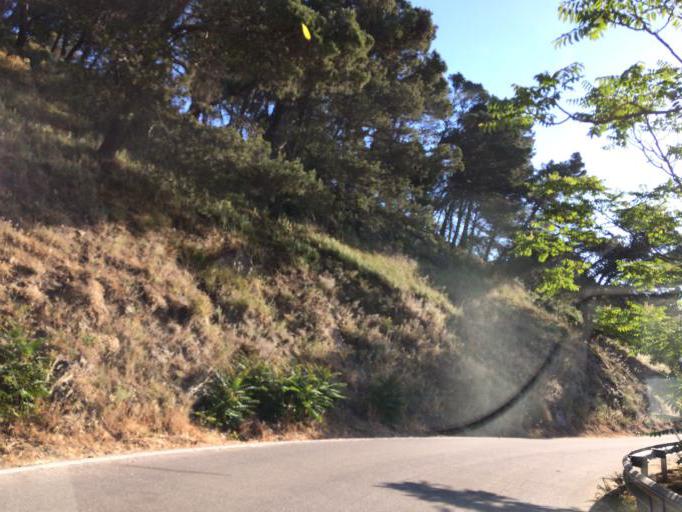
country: ES
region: Andalusia
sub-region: Provincia de Malaga
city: Colmenar
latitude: 36.8389
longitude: -4.3530
